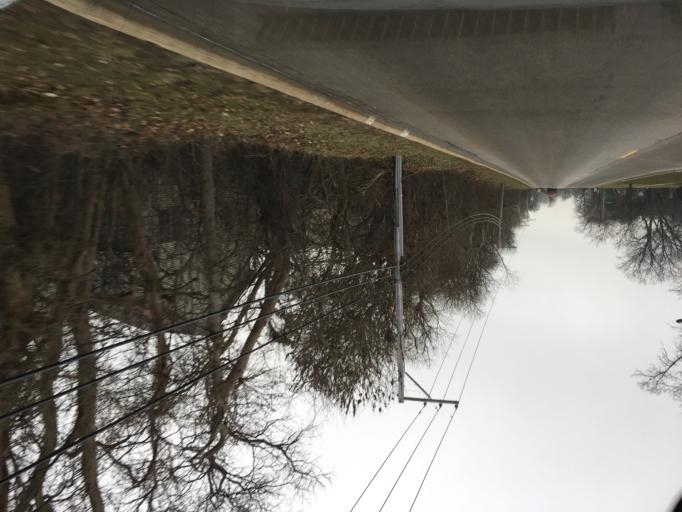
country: US
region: Illinois
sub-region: McHenry County
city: Lakewood
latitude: 42.2190
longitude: -88.3422
